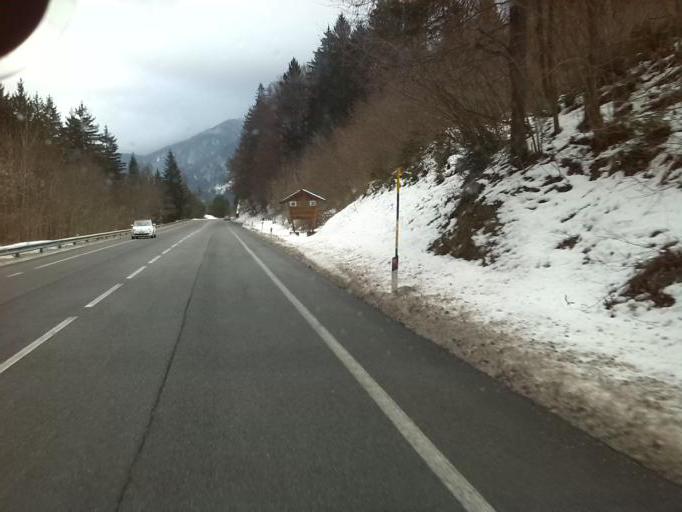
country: IT
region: Friuli Venezia Giulia
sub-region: Provincia di Udine
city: Pontebba
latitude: 46.5069
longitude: 13.3610
